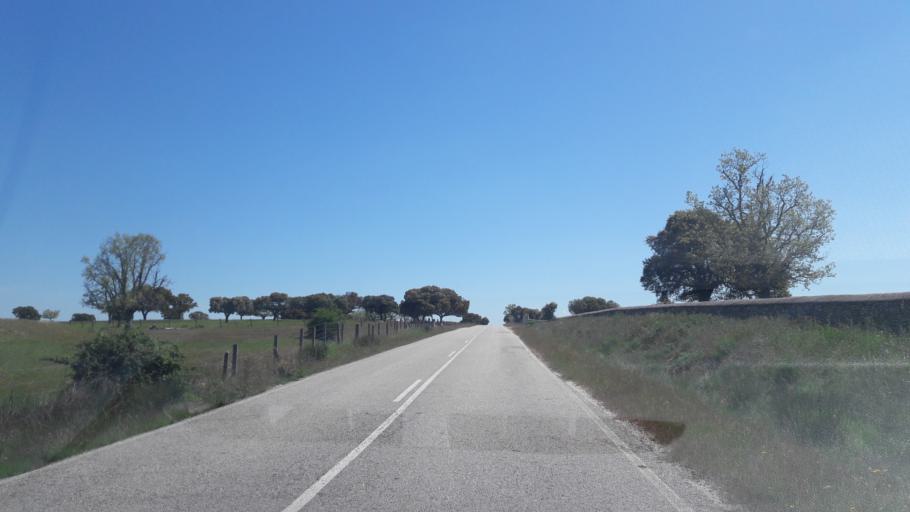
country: ES
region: Castille and Leon
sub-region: Provincia de Salamanca
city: Villarmuerto
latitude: 41.0488
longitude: -6.3815
